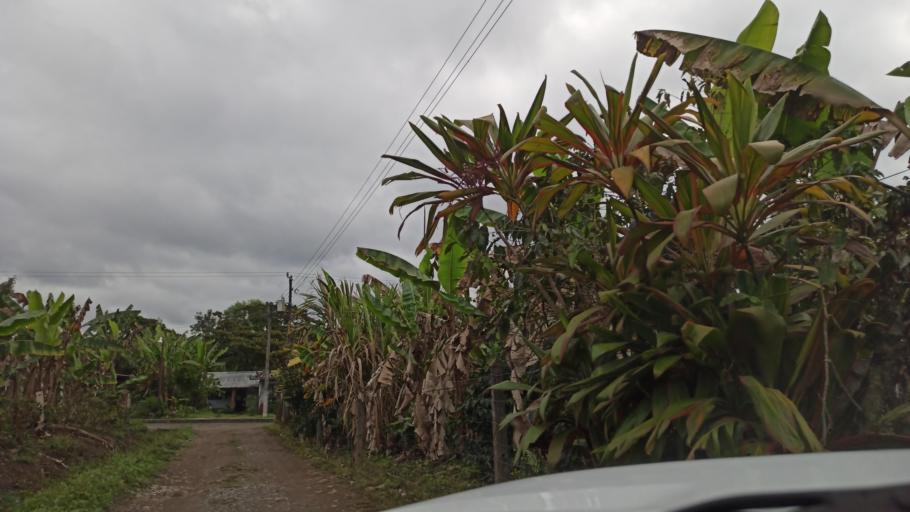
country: MX
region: Veracruz
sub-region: Chocaman
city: San Jose Neria
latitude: 18.9936
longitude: -96.9999
